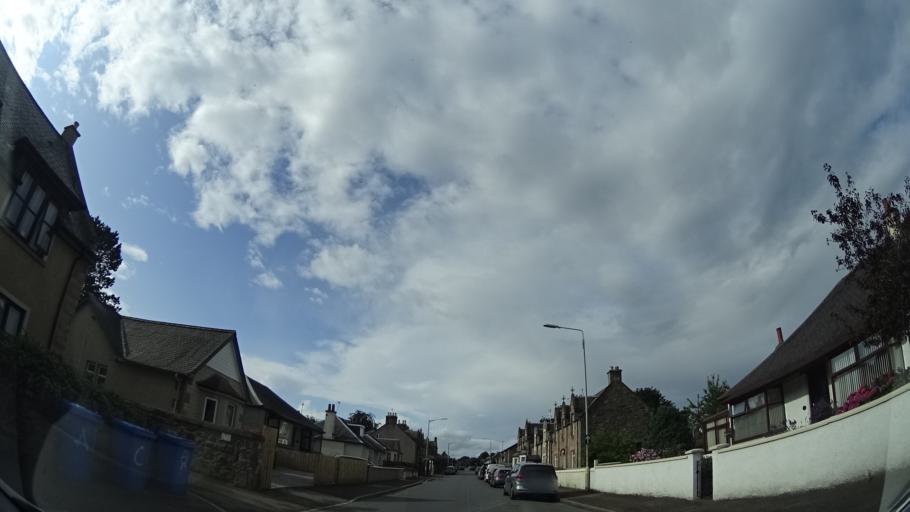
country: GB
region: Scotland
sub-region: Highland
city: Inverness
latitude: 57.4818
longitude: -4.2382
